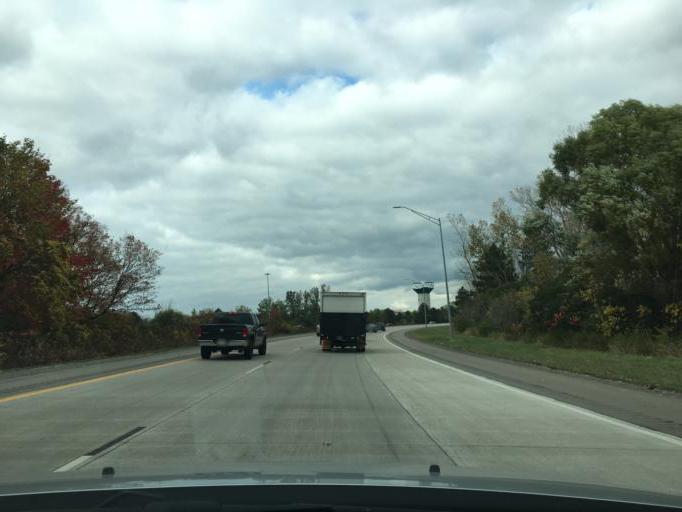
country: US
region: Michigan
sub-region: Oakland County
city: Farmington Hills
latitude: 42.4856
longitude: -83.4262
